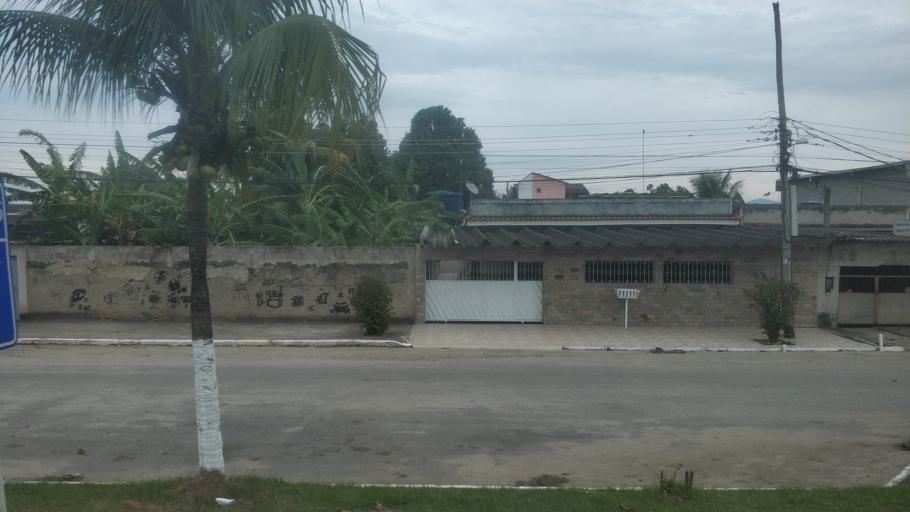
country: BR
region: Rio de Janeiro
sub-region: Seropedica
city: Seropedica
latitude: -22.7920
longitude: -43.6507
